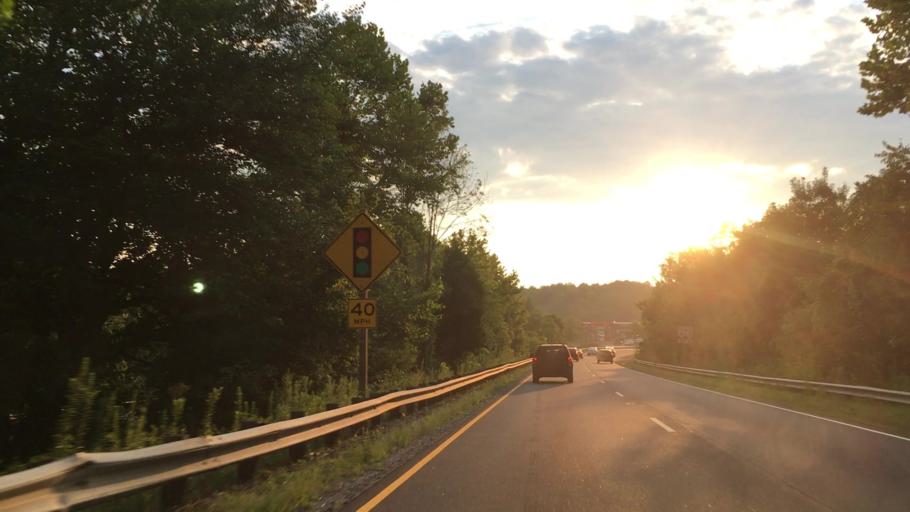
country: US
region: Virginia
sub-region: Spotsylvania County
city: Spotsylvania
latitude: 38.3253
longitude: -77.7246
